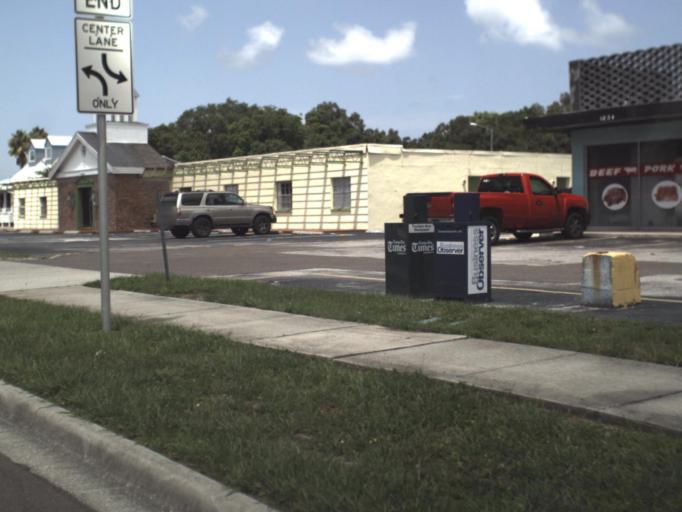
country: US
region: Florida
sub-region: Pinellas County
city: Clearwater
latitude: 27.9681
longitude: -82.7612
